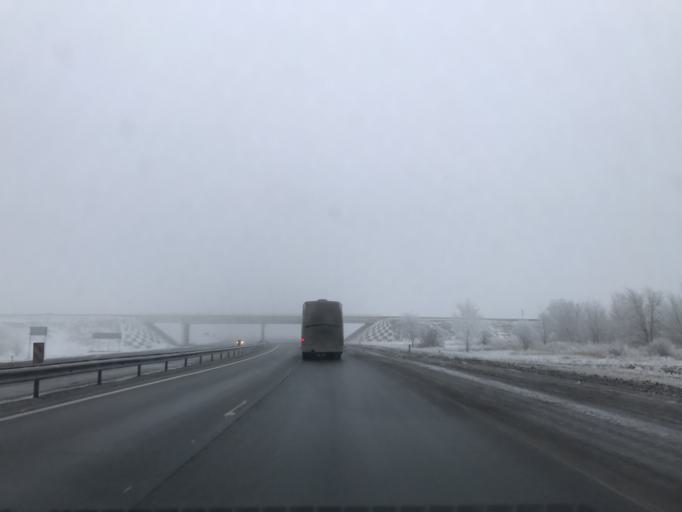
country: RU
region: Rostov
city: Grushevskaya
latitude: 47.4089
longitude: 39.9737
